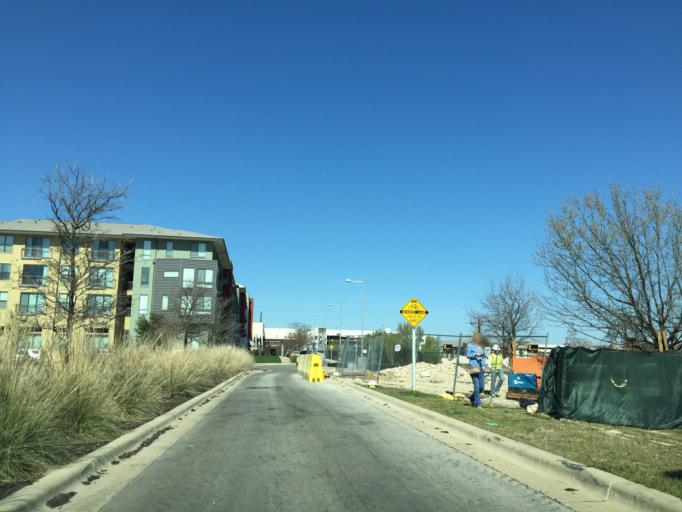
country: US
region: Texas
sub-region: Williamson County
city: Jollyville
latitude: 30.3953
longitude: -97.7256
